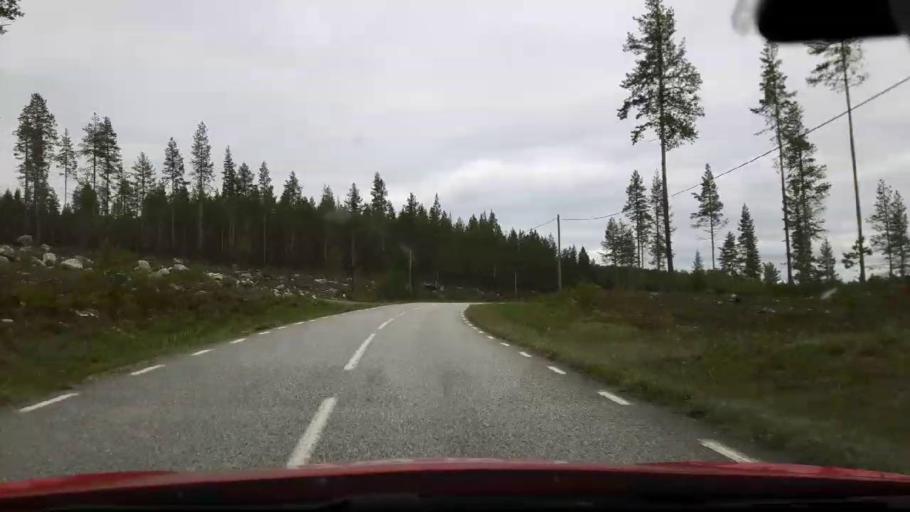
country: SE
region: Jaemtland
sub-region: Stroemsunds Kommun
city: Stroemsund
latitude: 63.3591
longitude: 15.7178
